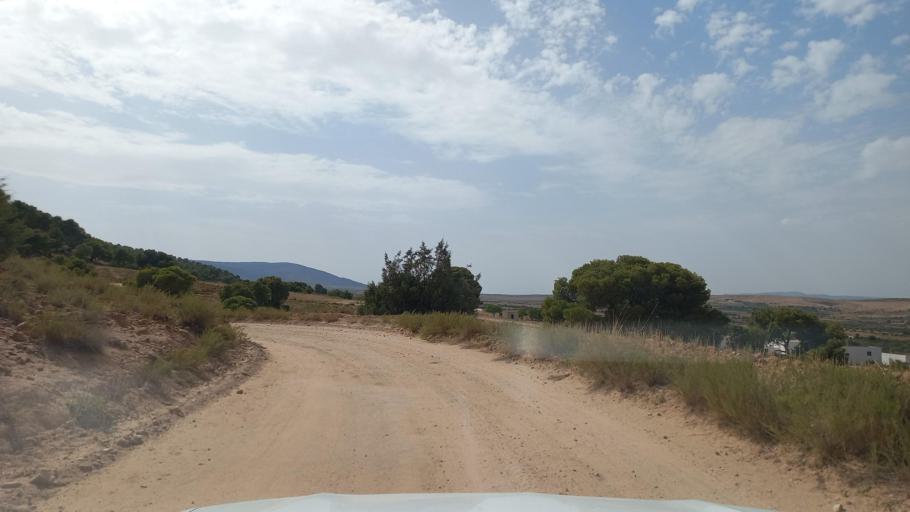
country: TN
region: Al Qasrayn
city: Kasserine
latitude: 35.3519
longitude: 8.8835
